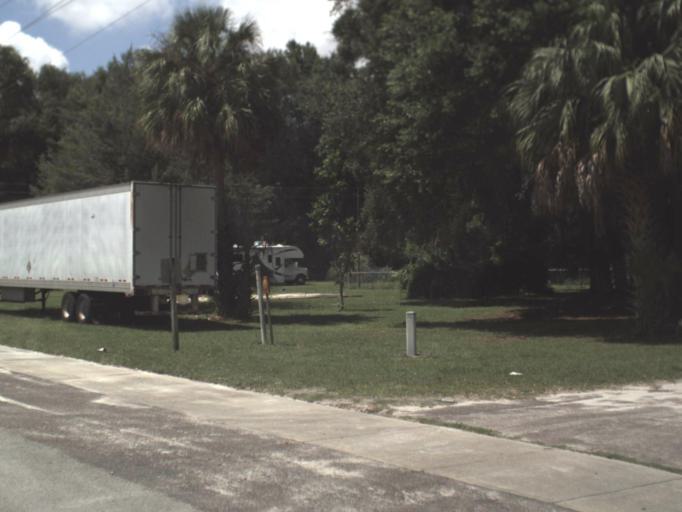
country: US
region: Florida
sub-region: Gilchrist County
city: Trenton
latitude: 29.7495
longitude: -82.8601
